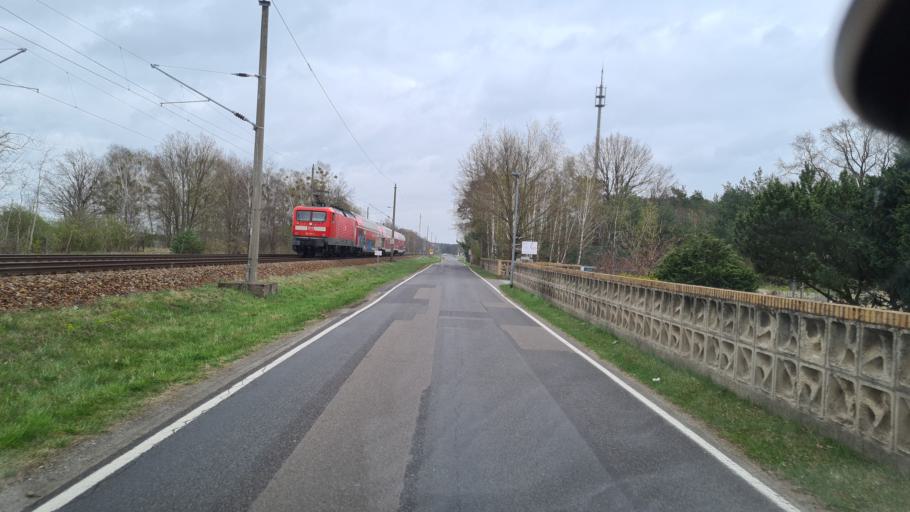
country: DE
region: Brandenburg
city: Ruhland
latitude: 51.4586
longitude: 13.8853
